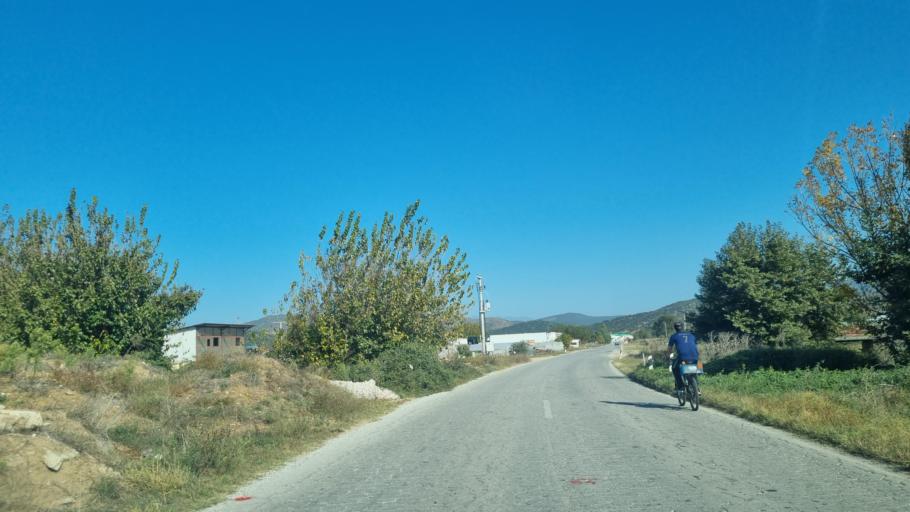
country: MK
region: Bogdanci
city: Bogdanci
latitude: 41.1943
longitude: 22.5717
